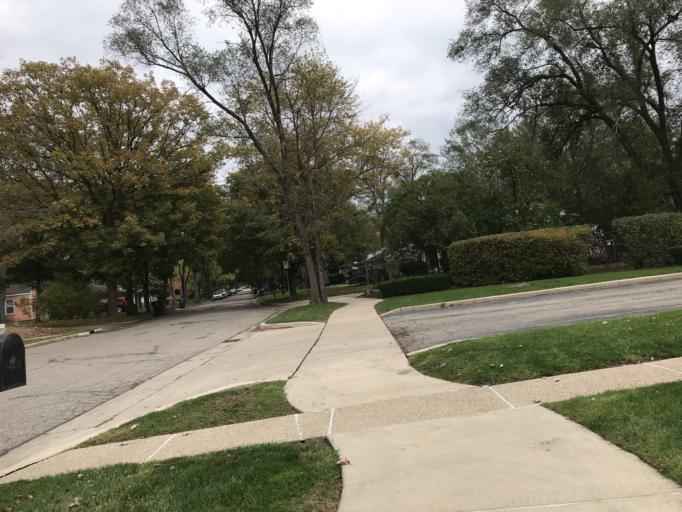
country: US
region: Michigan
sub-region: Washtenaw County
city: Ann Arbor
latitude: 42.2549
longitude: -83.7324
